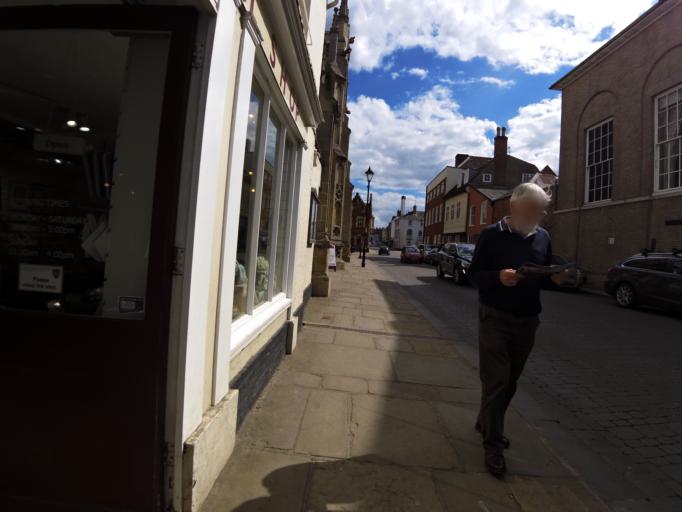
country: GB
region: England
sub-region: Suffolk
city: Bury St Edmunds
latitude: 52.2441
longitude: 0.7164
